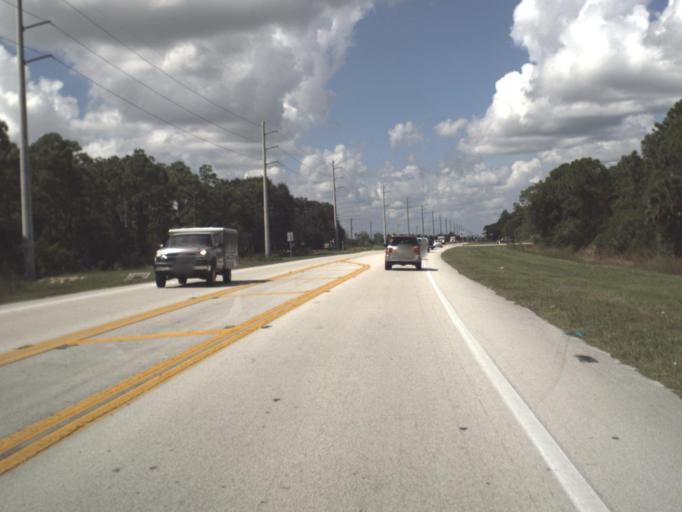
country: US
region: Florida
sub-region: Lee County
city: Gateway
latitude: 26.5925
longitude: -81.7376
